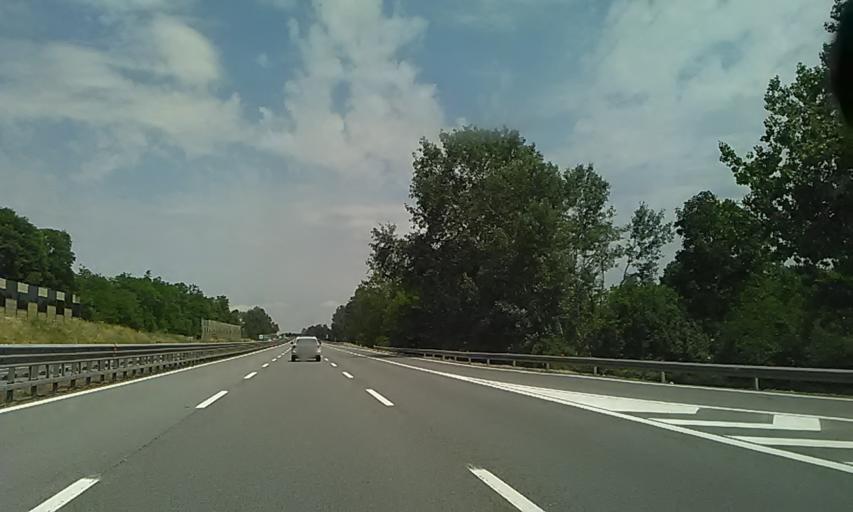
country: IT
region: Piedmont
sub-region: Provincia di Alessandria
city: Silvano d'Orba
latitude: 44.6811
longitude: 8.6604
